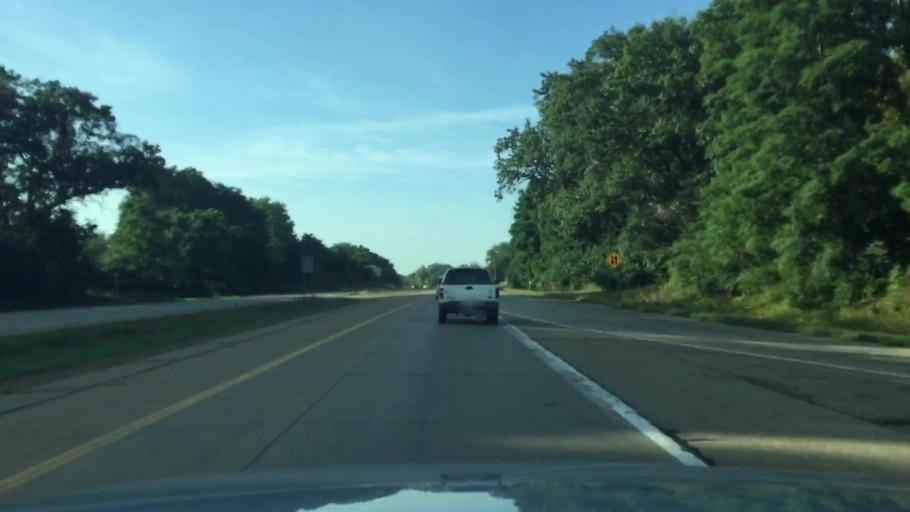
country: US
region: Michigan
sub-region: Jackson County
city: Vandercook Lake
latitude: 42.1945
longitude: -84.3698
